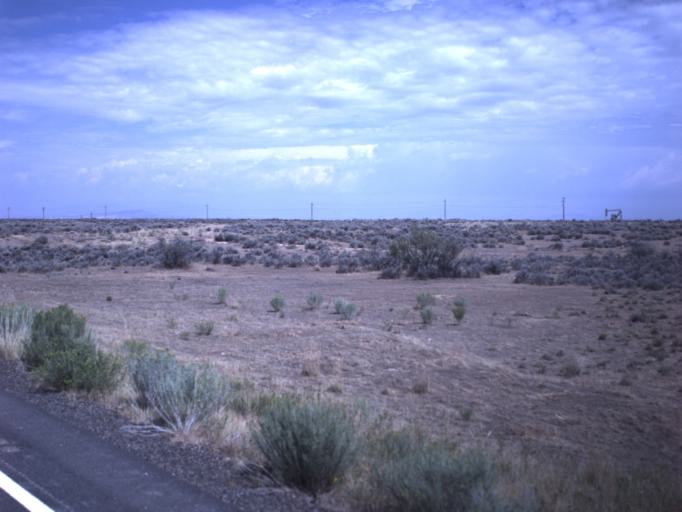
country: US
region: Utah
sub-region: Uintah County
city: Naples
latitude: 40.2001
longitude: -109.3465
